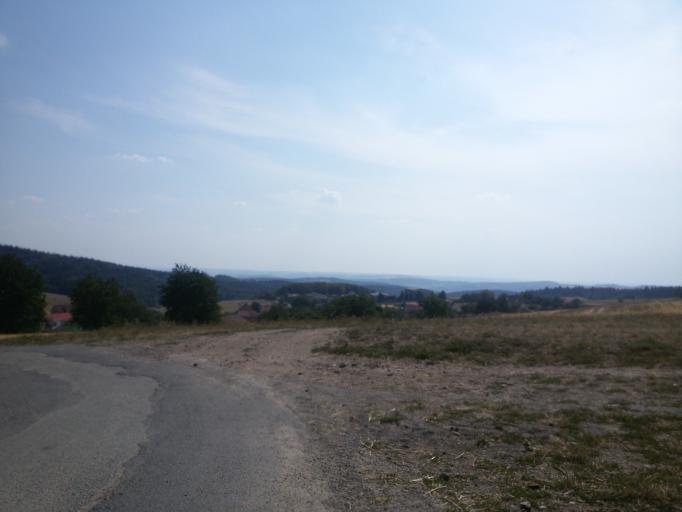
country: CZ
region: South Moravian
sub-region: Okres Brno-Venkov
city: Lomnice
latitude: 49.4460
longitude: 16.4587
